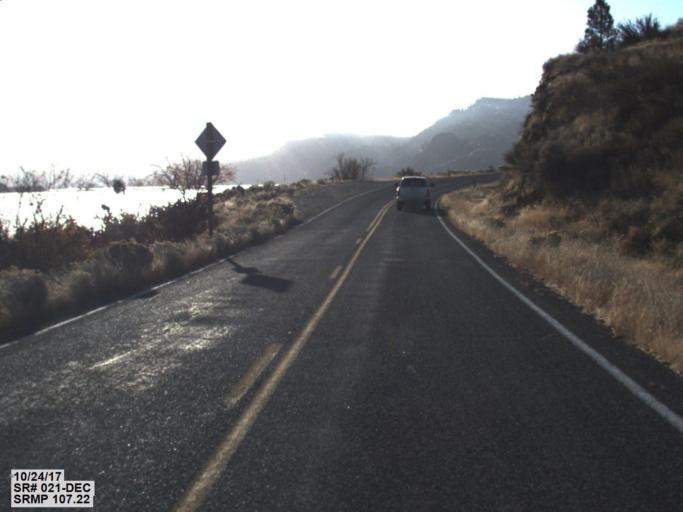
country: US
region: Washington
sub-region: Okanogan County
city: Coulee Dam
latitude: 47.9545
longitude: -118.6925
